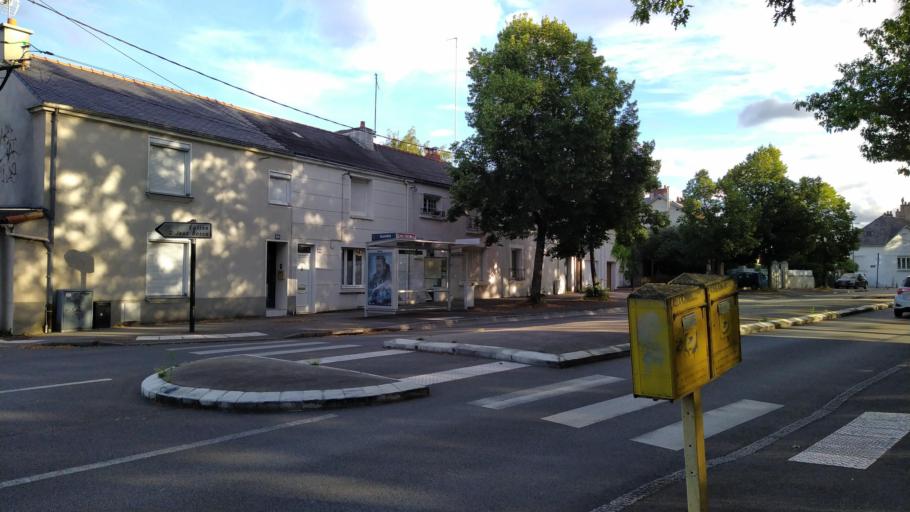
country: FR
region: Pays de la Loire
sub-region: Departement de la Loire-Atlantique
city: Nantes
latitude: 47.2398
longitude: -1.5373
